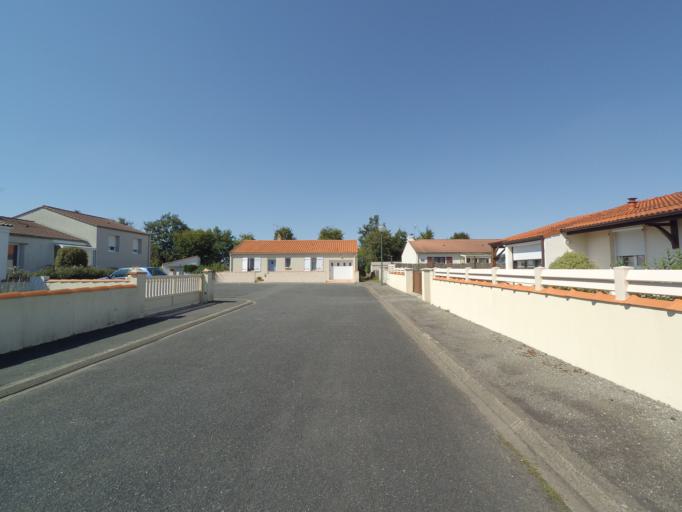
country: FR
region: Pays de la Loire
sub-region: Departement de la Loire-Atlantique
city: Vieillevigne
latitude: 46.9697
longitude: -1.4424
